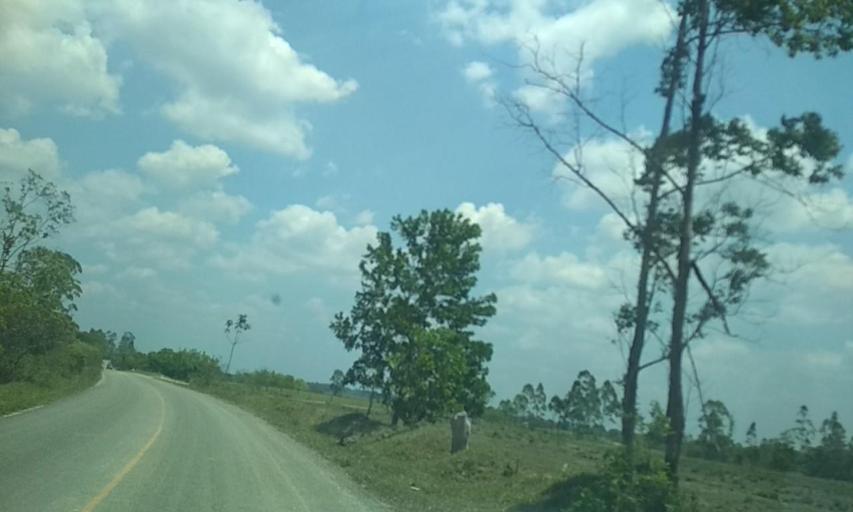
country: MX
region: Tabasco
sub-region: Huimanguillo
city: Francisco Rueda
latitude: 17.8083
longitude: -93.8672
